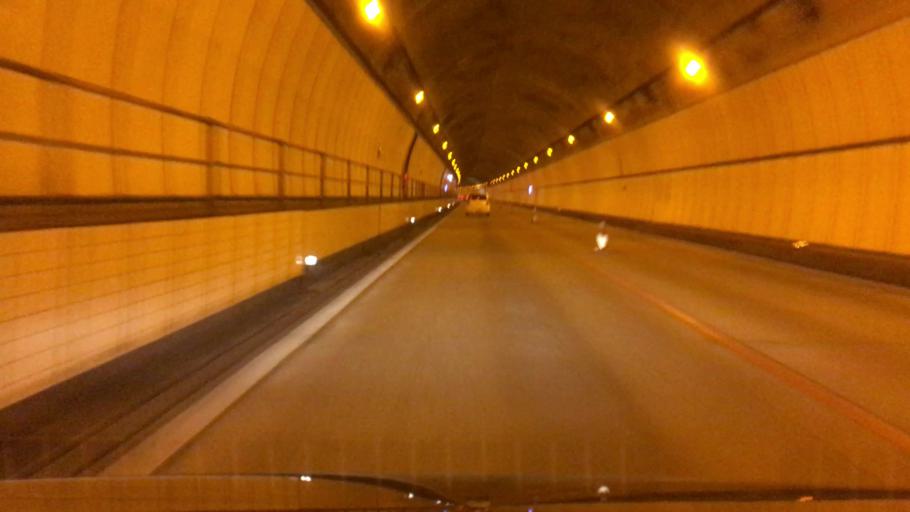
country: JP
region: Hyogo
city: Sasayama
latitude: 35.1201
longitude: 135.1650
